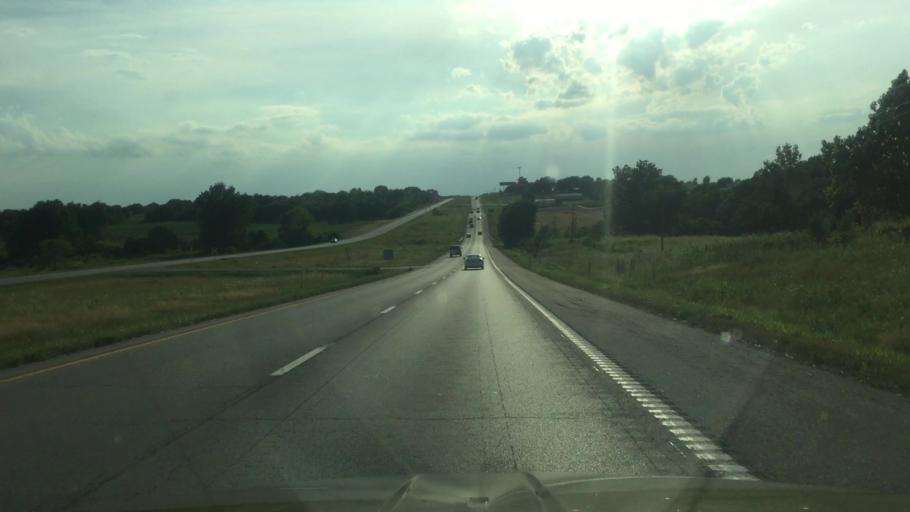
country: US
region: Missouri
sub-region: Jackson County
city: Lone Jack
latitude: 38.8693
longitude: -94.0980
